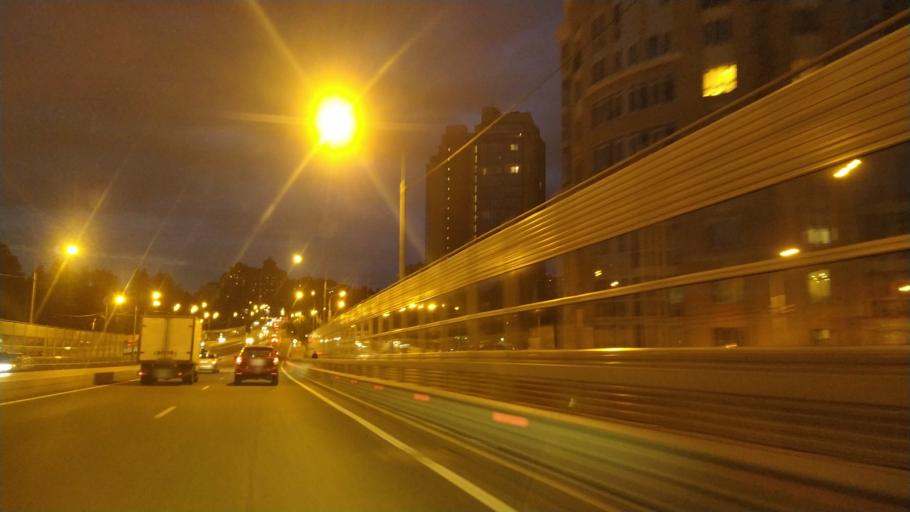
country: RU
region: Leningrad
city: Udel'naya
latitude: 60.0268
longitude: 30.3126
